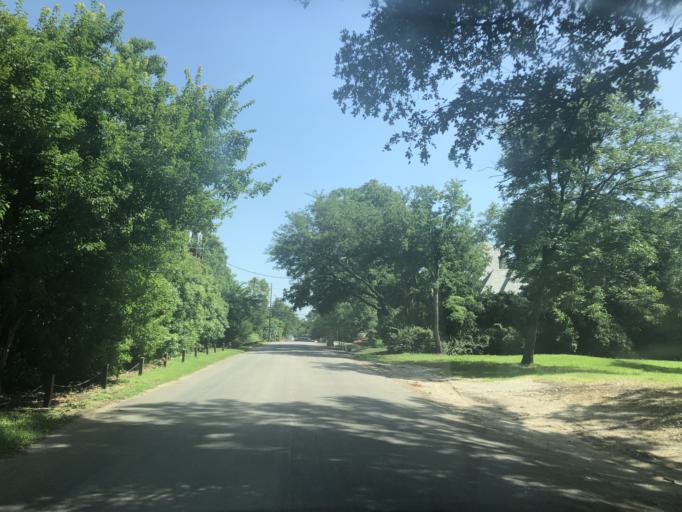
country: US
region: Texas
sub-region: Dallas County
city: University Park
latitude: 32.8789
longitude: -96.8139
